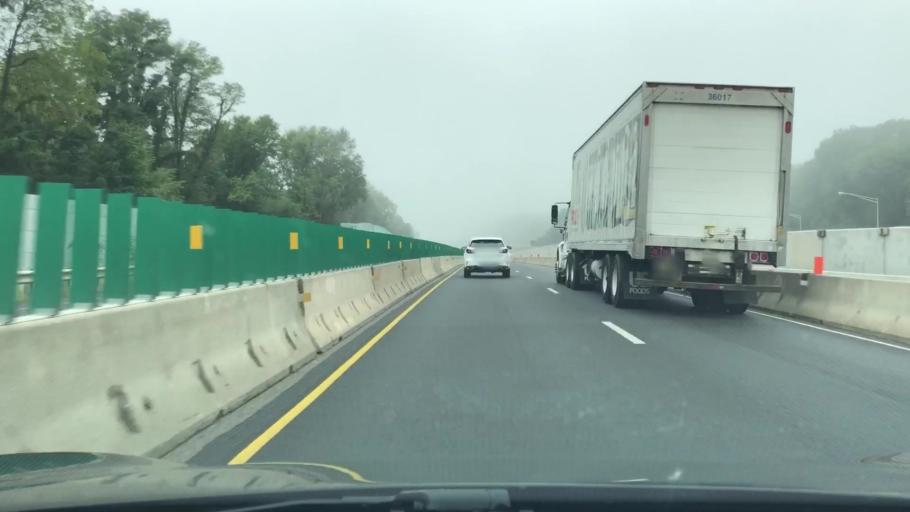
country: US
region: Pennsylvania
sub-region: Bucks County
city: Yardley
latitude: 40.2525
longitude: -74.8634
